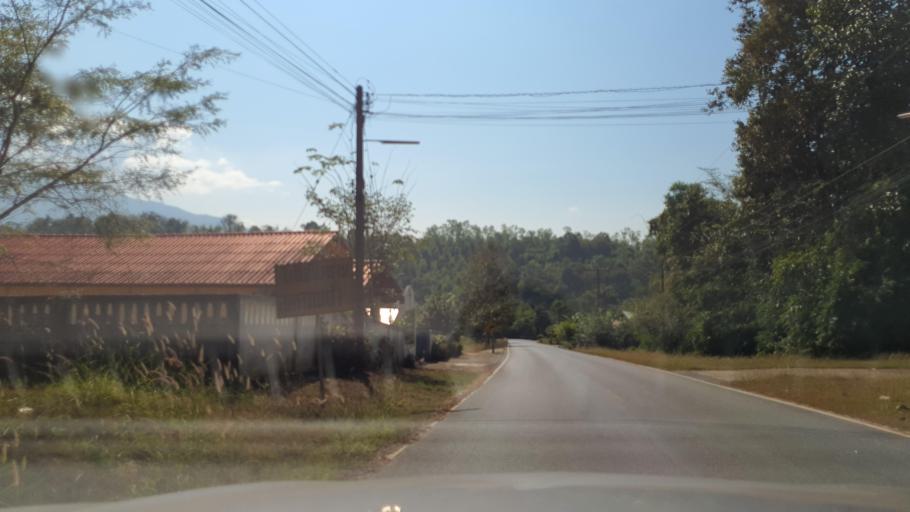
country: TH
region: Nan
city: Pua
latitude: 19.1148
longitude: 100.9130
